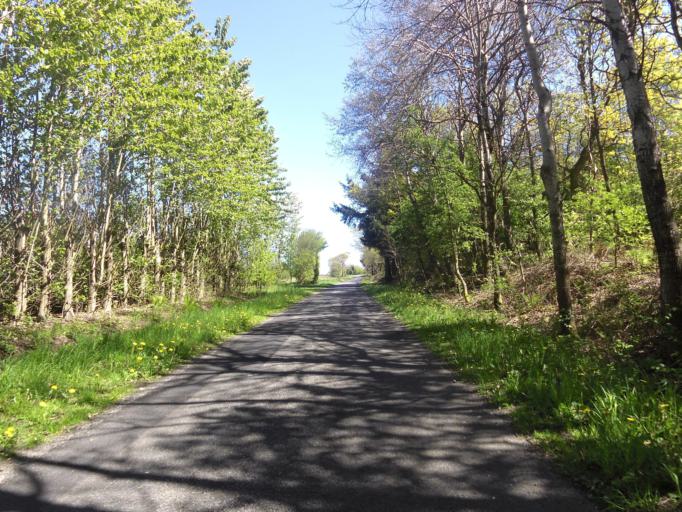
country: DK
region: South Denmark
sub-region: Tonder Kommune
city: Sherrebek
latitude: 55.2360
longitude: 8.7278
